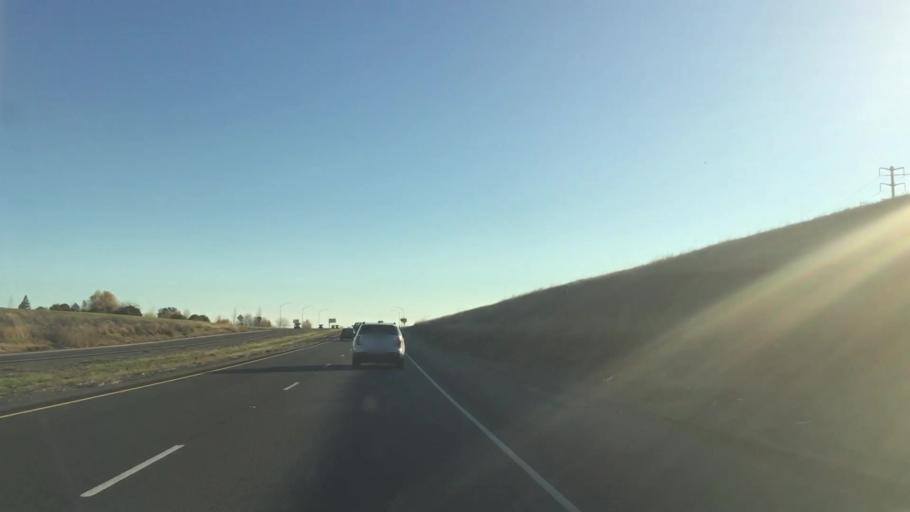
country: US
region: California
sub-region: Yuba County
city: Olivehurst
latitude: 39.0768
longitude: -121.5414
